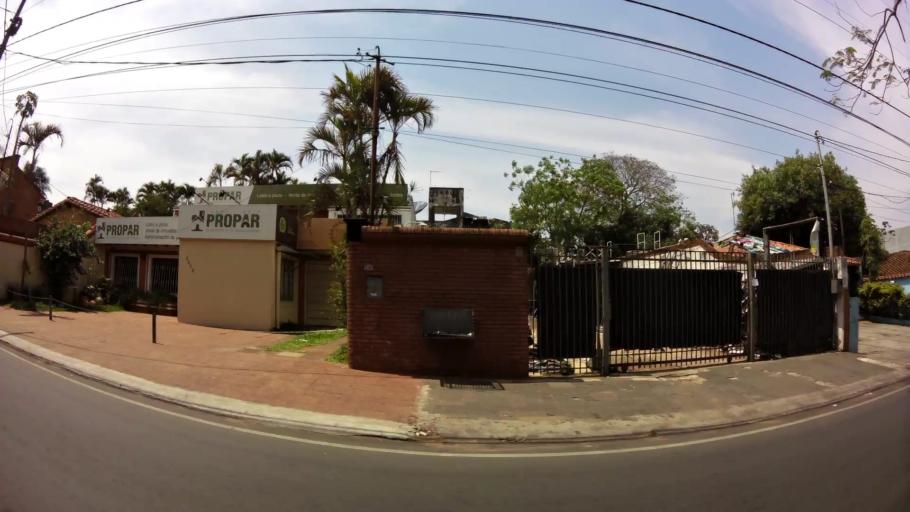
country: PY
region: Central
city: Lambare
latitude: -25.3200
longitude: -57.5929
